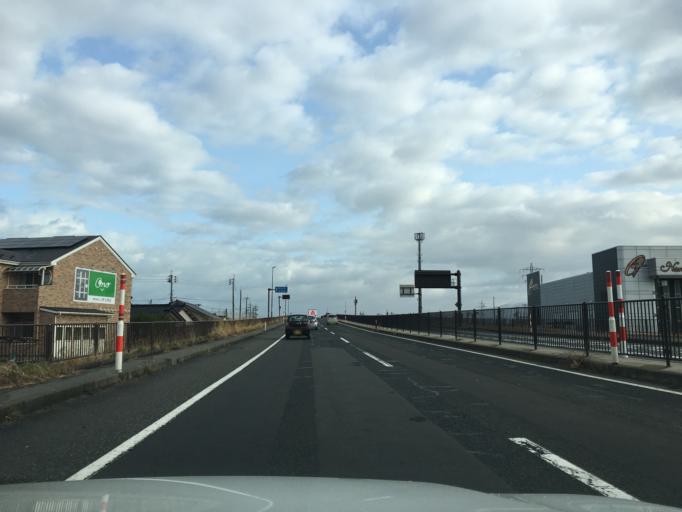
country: JP
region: Yamagata
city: Sakata
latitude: 38.9098
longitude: 139.8575
